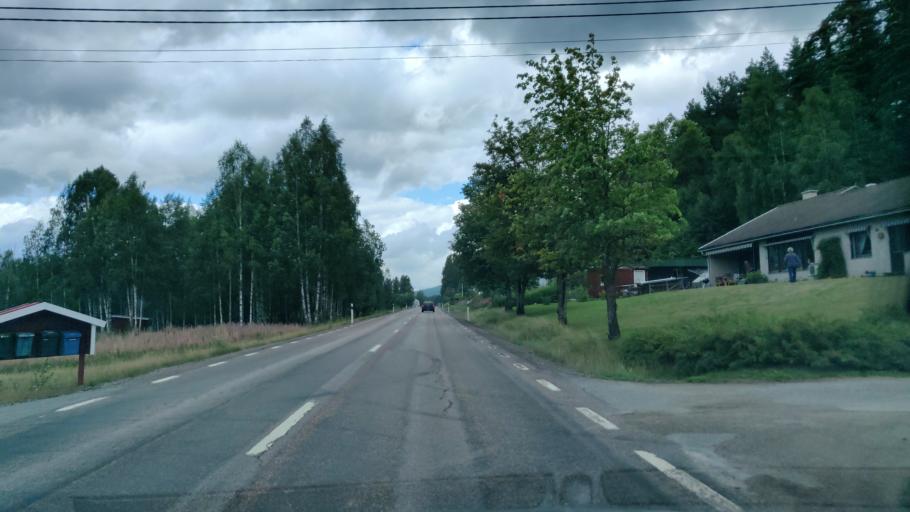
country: SE
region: Vaermland
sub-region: Torsby Kommun
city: Torsby
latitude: 60.5867
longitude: 13.0788
